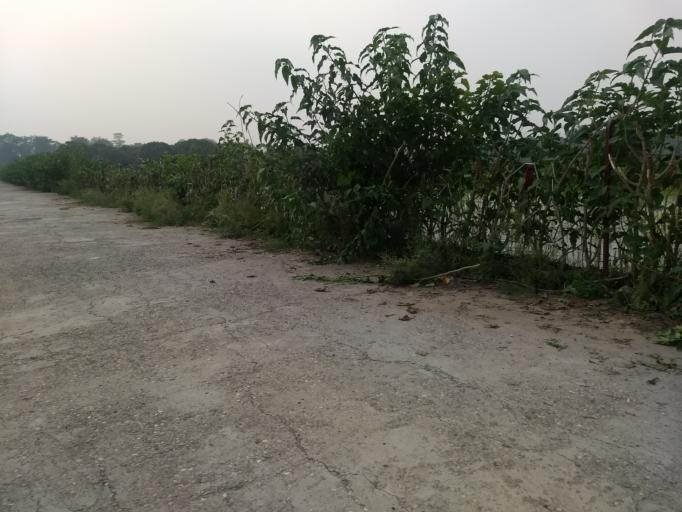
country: IN
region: Uttarakhand
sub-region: Dehradun
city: Raiwala
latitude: 30.0376
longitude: 78.2172
